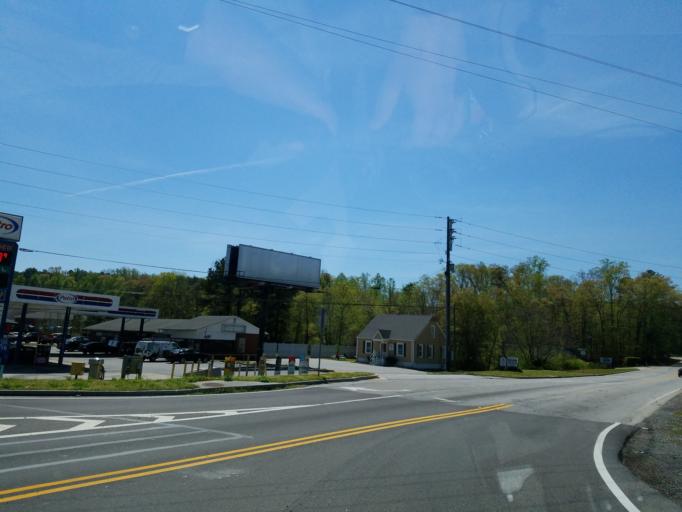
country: US
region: Georgia
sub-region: Paulding County
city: Hiram
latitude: 33.8702
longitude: -84.7649
